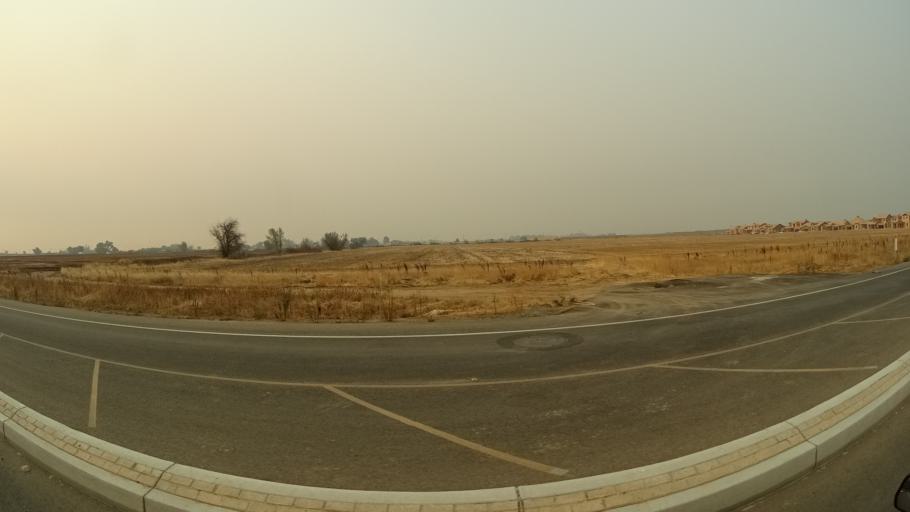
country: US
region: California
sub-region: Sacramento County
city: Laguna
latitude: 38.3797
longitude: -121.4085
